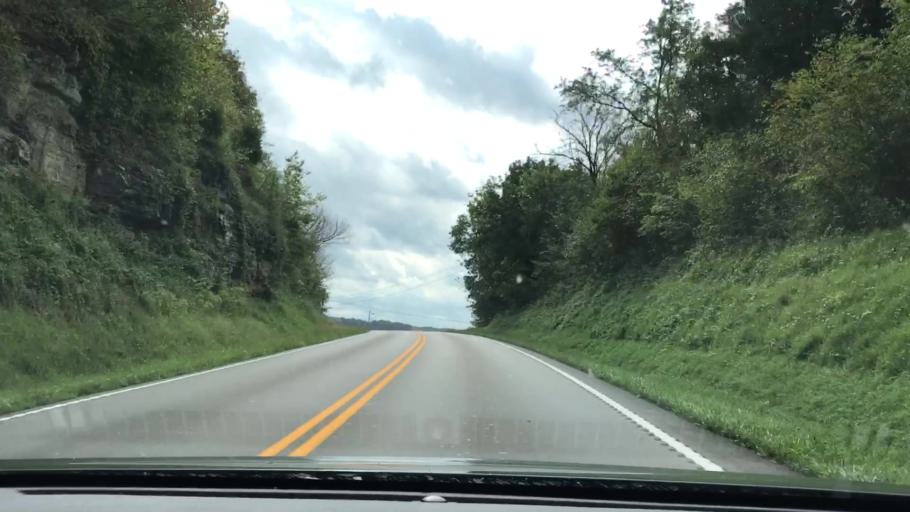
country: US
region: Kentucky
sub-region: Cumberland County
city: Burkesville
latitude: 36.8030
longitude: -85.4250
